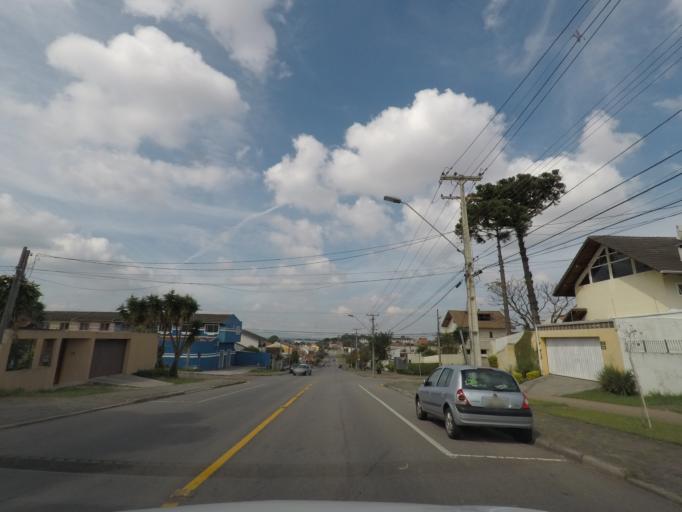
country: BR
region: Parana
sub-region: Pinhais
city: Pinhais
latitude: -25.4448
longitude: -49.2218
